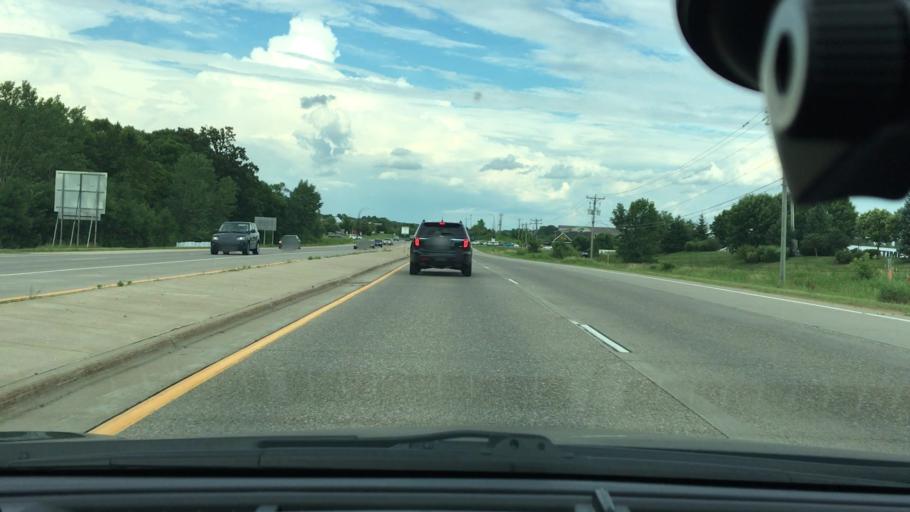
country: US
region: Minnesota
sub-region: Hennepin County
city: Shorewood
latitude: 44.8632
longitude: -93.5951
